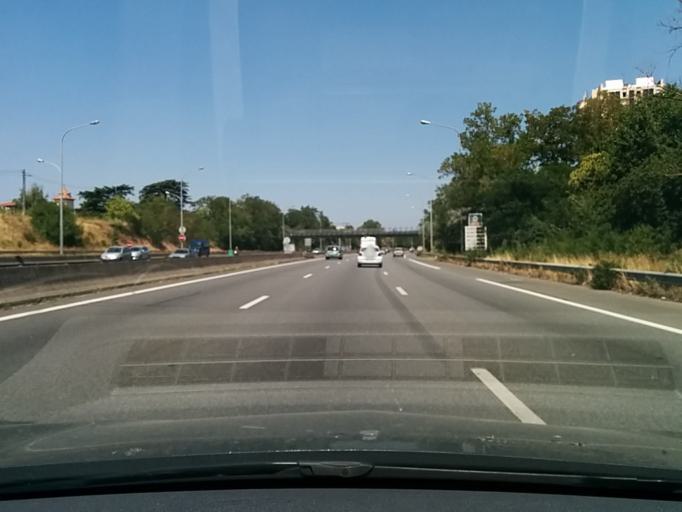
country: FR
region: Midi-Pyrenees
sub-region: Departement de la Haute-Garonne
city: Blagnac
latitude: 43.5942
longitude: 1.3978
